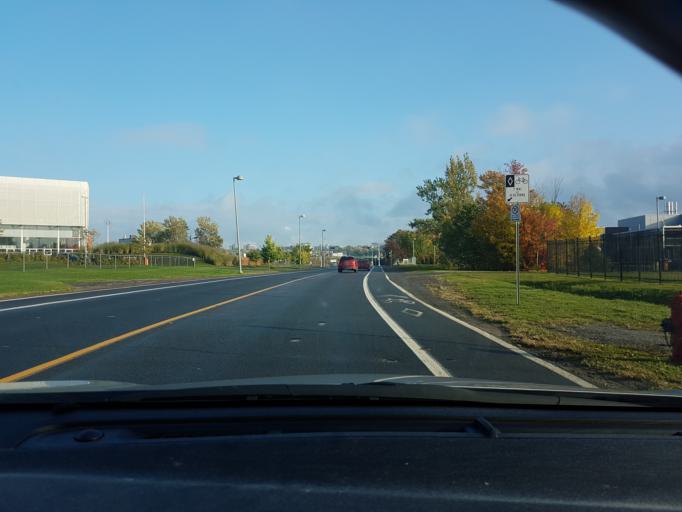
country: CA
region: Quebec
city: L'Ancienne-Lorette
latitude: 46.7973
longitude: -71.2955
